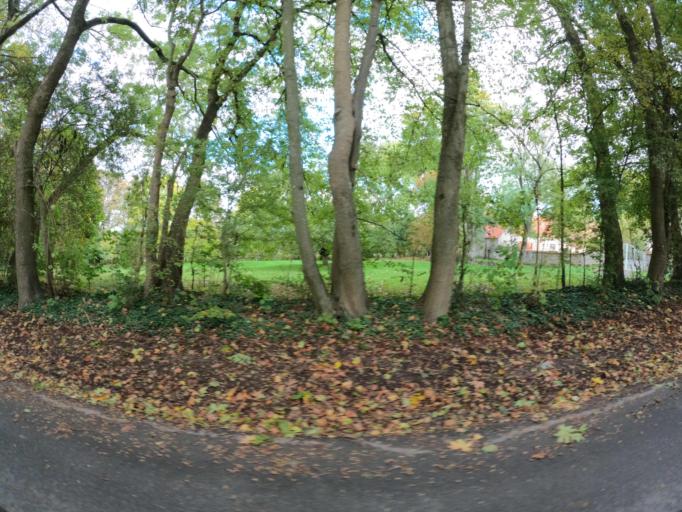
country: FR
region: Ile-de-France
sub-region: Departement de Seine-et-Marne
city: Coupvray
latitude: 48.8892
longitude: 2.8011
